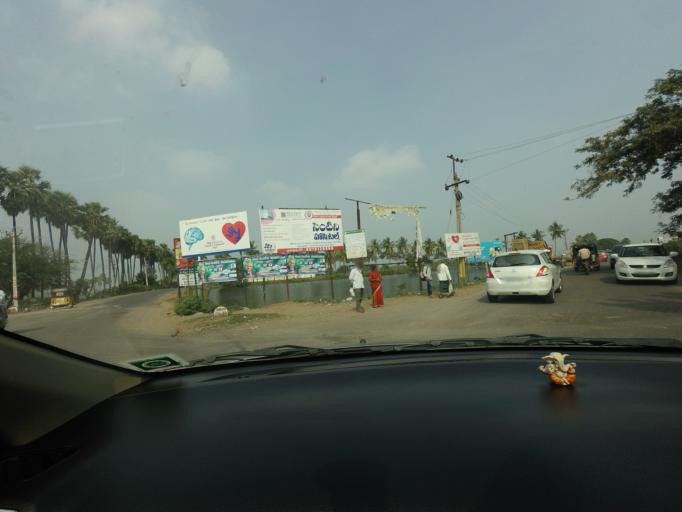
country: IN
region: Andhra Pradesh
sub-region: Krishna
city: Kankipadu
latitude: 16.4523
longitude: 80.7714
